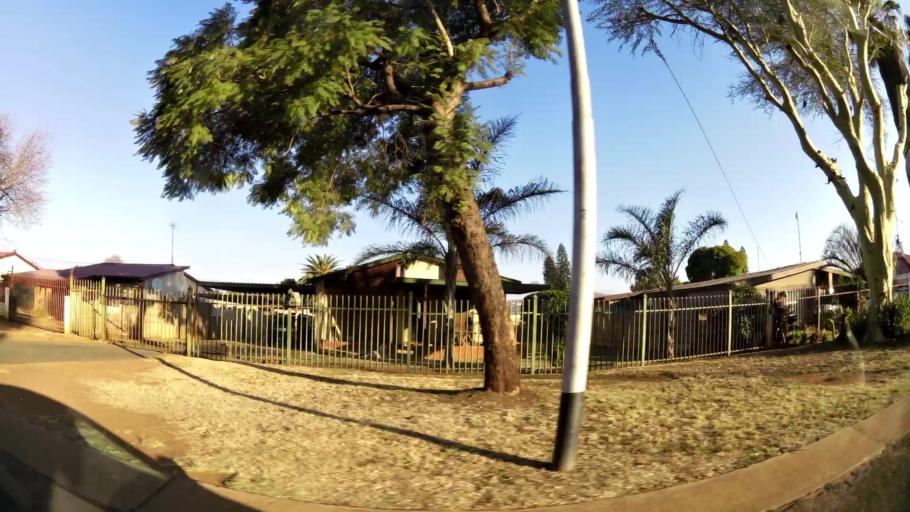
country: ZA
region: Gauteng
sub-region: City of Tshwane Metropolitan Municipality
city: Pretoria
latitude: -25.7361
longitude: 28.1182
